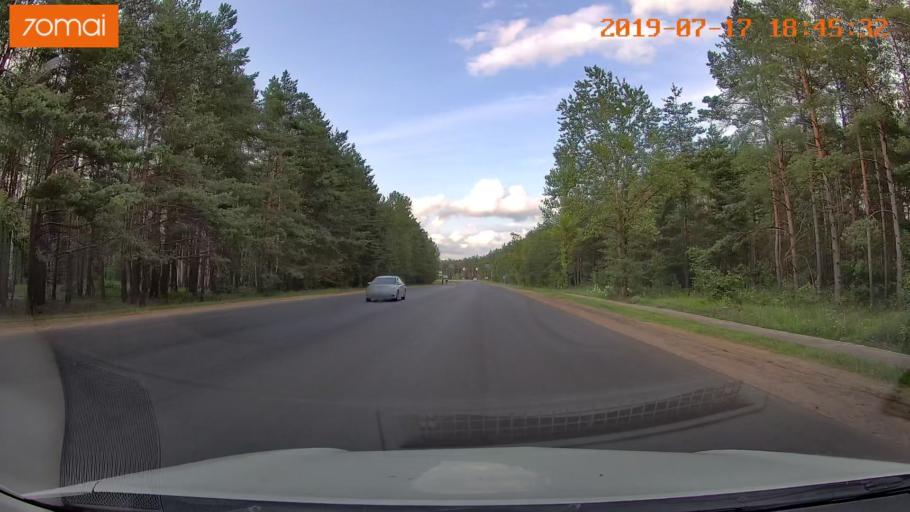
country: BY
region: Mogilev
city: Asipovichy
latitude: 53.3255
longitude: 28.6557
